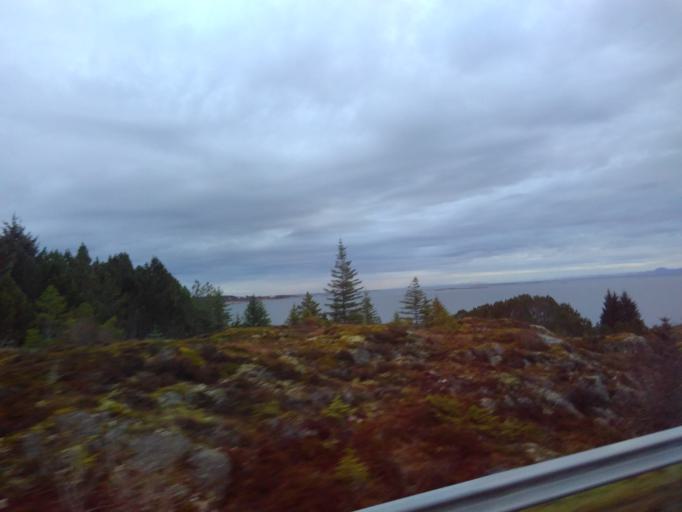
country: NO
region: Sor-Trondelag
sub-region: Froya
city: Sistranda
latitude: 63.7466
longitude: 8.8367
